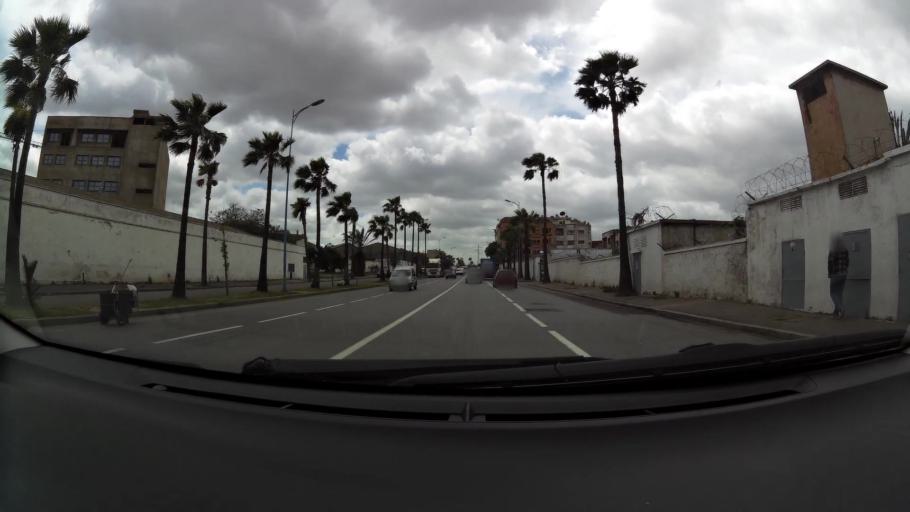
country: MA
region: Grand Casablanca
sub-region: Casablanca
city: Casablanca
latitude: 33.5897
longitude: -7.5458
